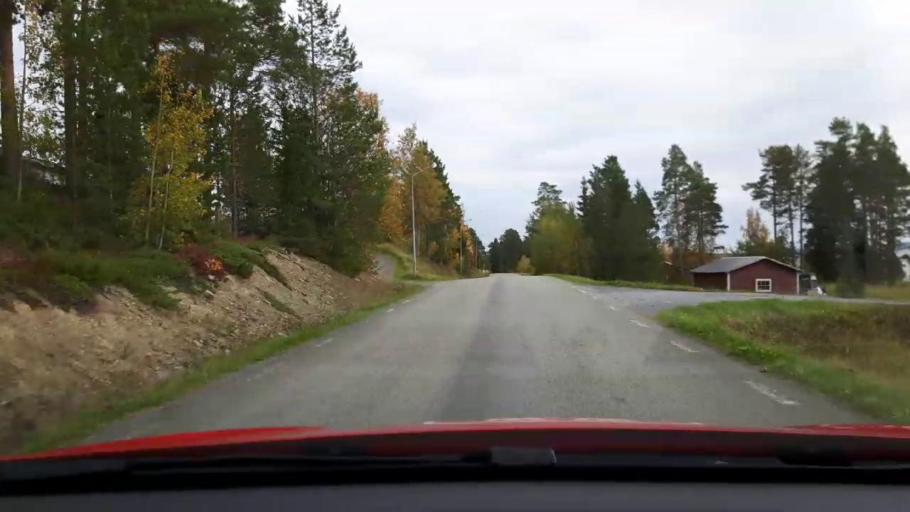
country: SE
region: Jaemtland
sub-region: Krokoms Kommun
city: Valla
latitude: 63.2579
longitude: 14.0167
